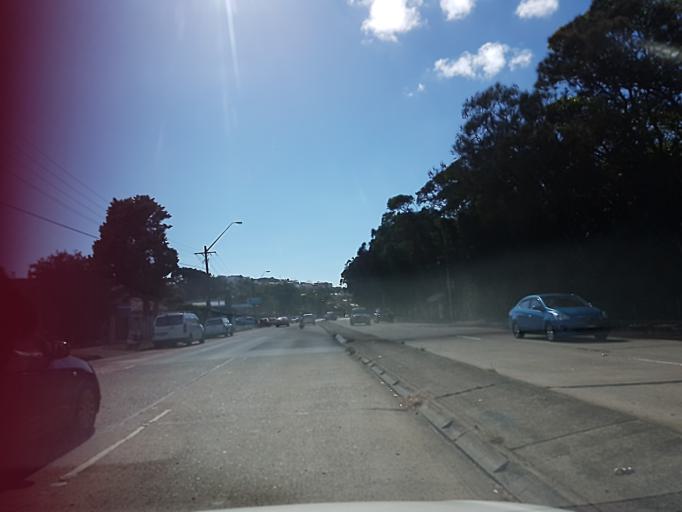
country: AU
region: New South Wales
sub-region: Warringah
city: Dee Why
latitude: -33.7454
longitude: 151.2932
